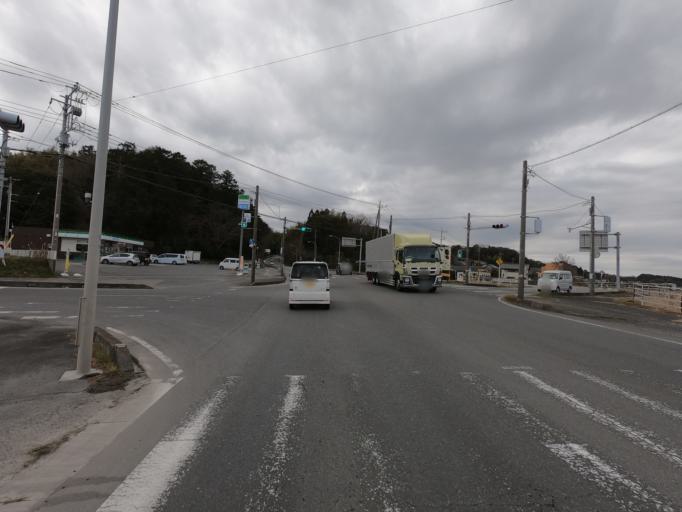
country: JP
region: Ibaraki
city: Ishioka
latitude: 36.0918
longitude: 140.3788
